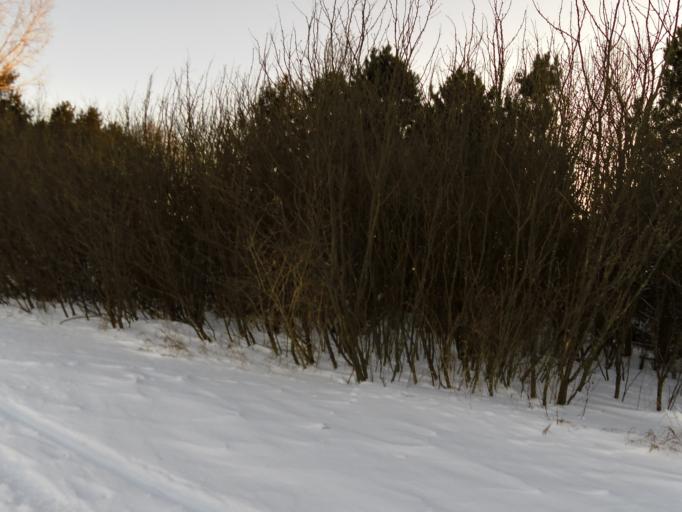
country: US
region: Minnesota
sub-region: Washington County
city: Lake Elmo
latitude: 44.9721
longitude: -92.9182
